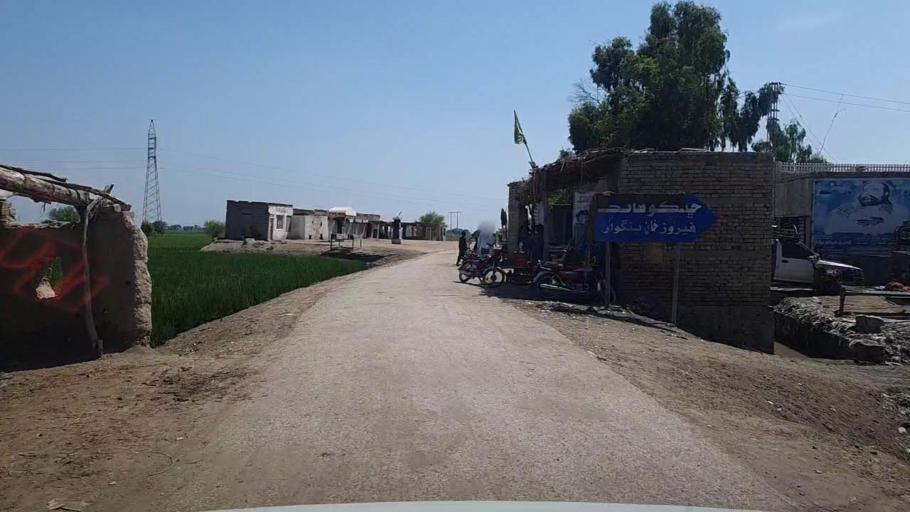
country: PK
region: Sindh
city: Kandhkot
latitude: 28.3191
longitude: 69.3400
